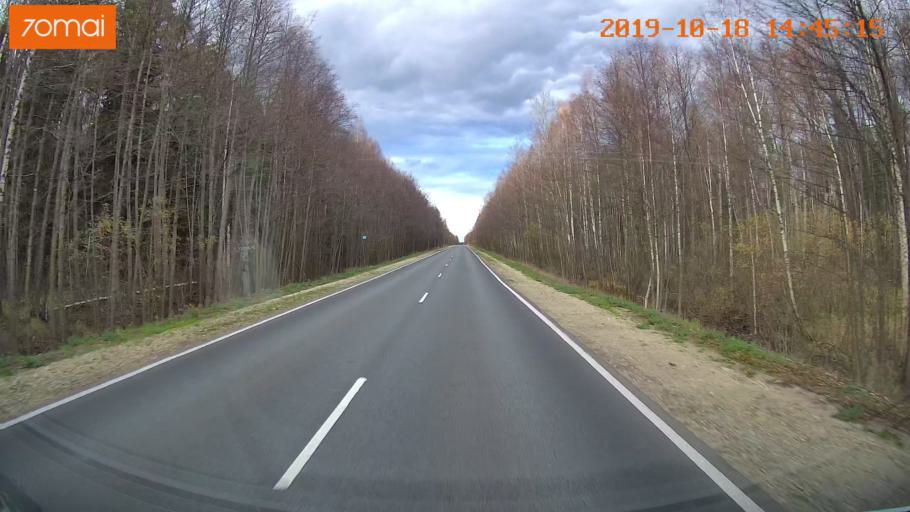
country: RU
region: Vladimir
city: Velikodvorskiy
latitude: 55.3518
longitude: 40.6785
